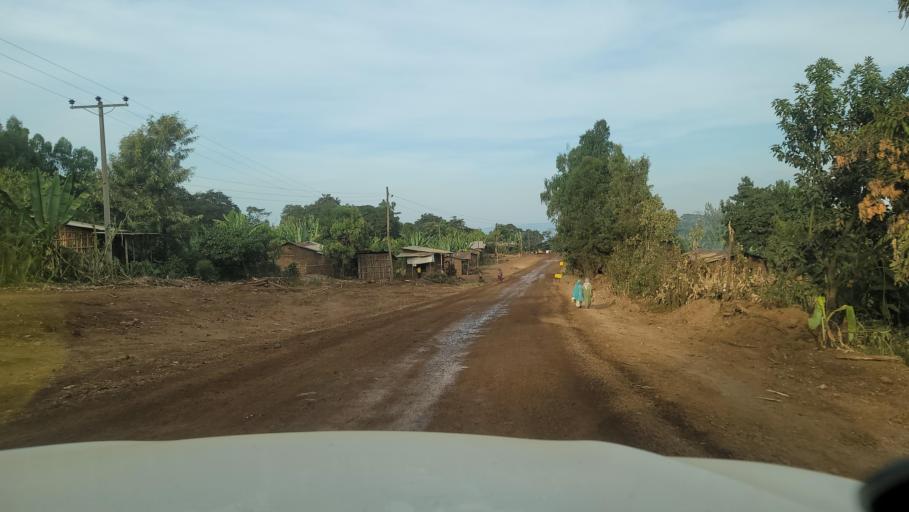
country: ET
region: Oromiya
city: Agaro
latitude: 7.8246
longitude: 36.5395
